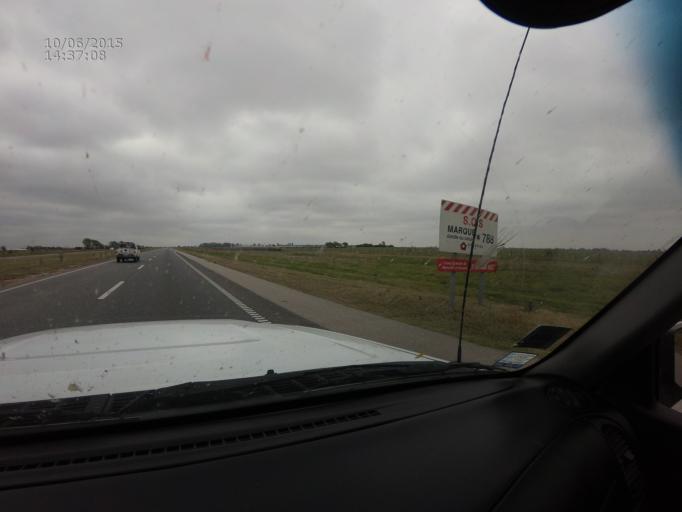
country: AR
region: Cordoba
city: James Craik
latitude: -32.1121
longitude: -63.4567
